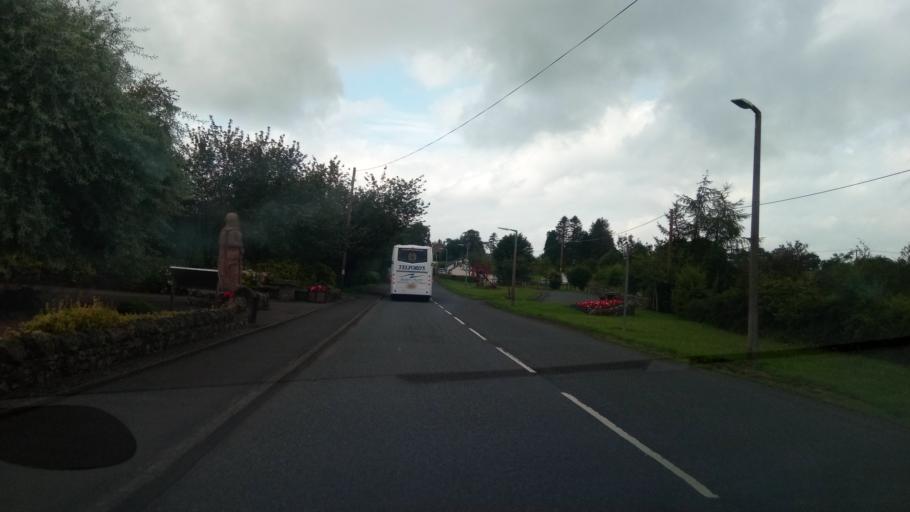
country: GB
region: Scotland
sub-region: Dumfries and Galloway
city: Langholm
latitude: 55.0862
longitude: -2.9272
